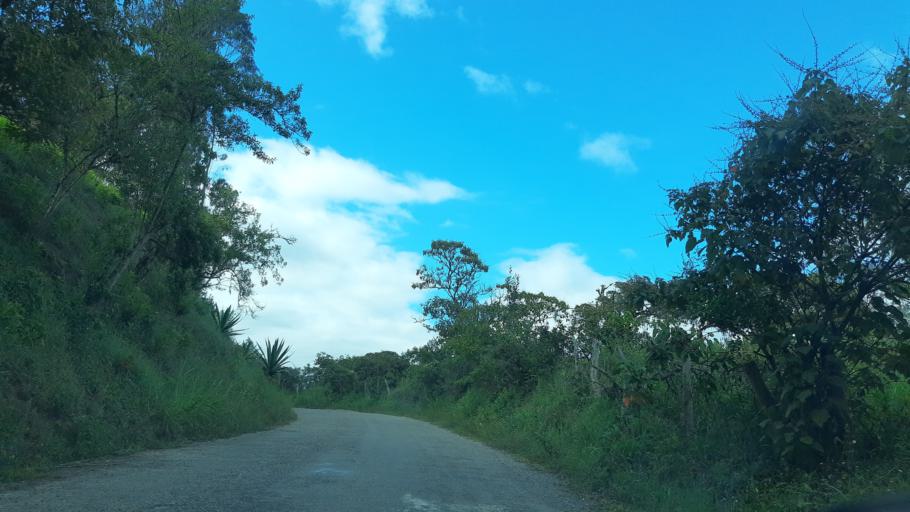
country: CO
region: Cundinamarca
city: Tenza
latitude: 5.0457
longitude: -73.4206
